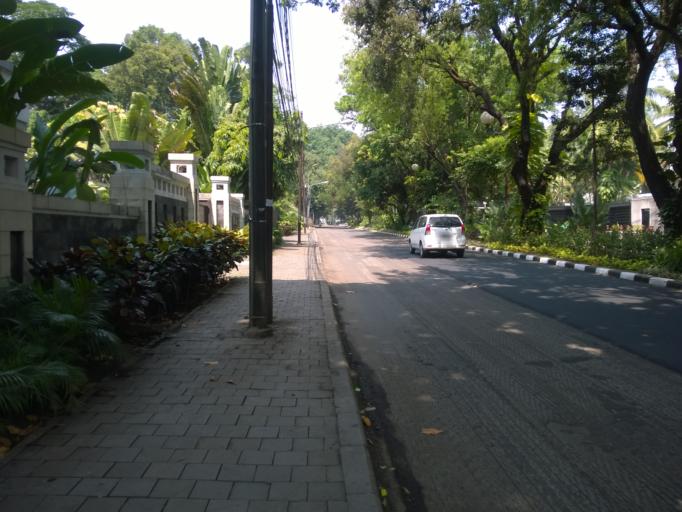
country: ID
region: Jakarta Raya
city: Jakarta
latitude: -6.1972
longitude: 106.8330
